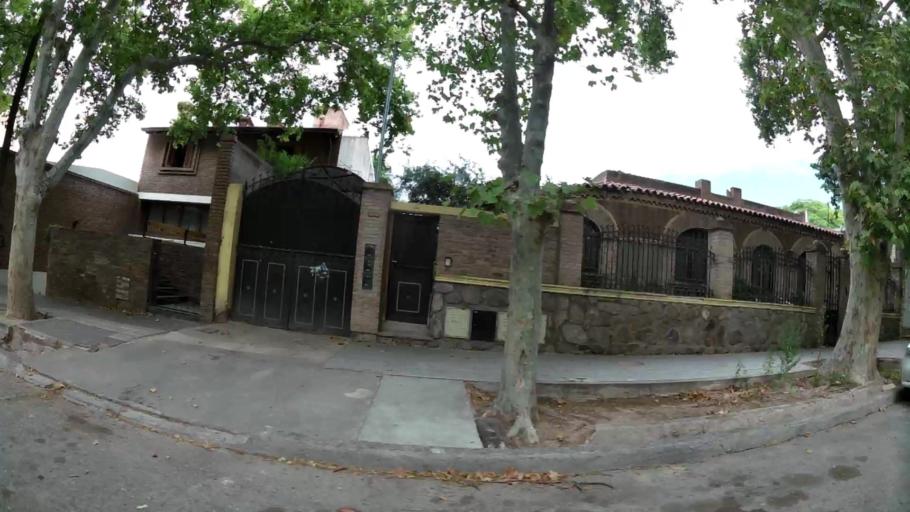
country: AR
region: Mendoza
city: Mendoza
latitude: -32.8757
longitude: -68.8584
